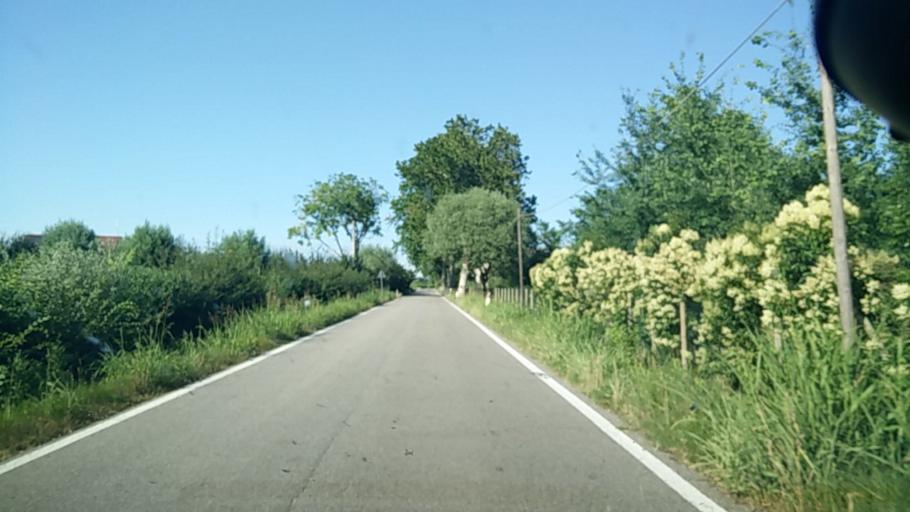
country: IT
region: Veneto
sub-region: Provincia di Treviso
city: Monastier di Treviso
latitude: 45.6629
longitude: 12.4231
